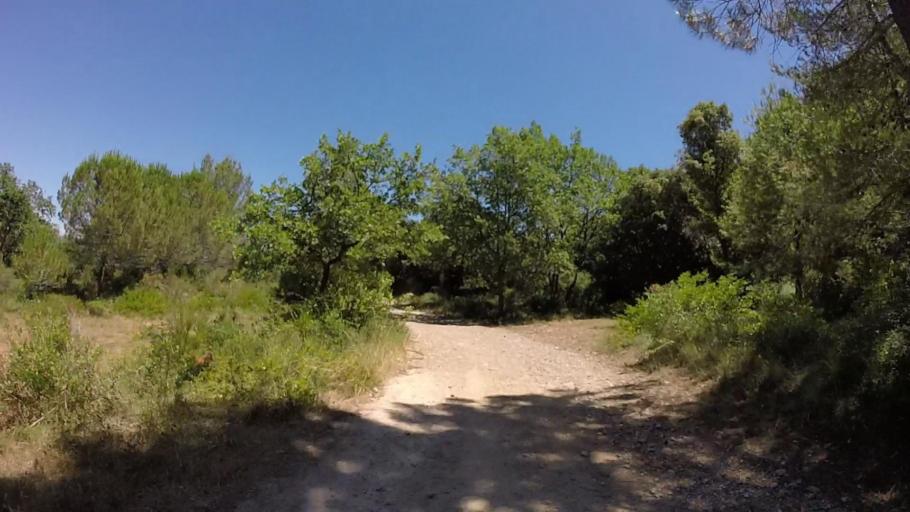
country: FR
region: Provence-Alpes-Cote d'Azur
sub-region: Departement des Alpes-Maritimes
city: Biot
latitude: 43.6303
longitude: 7.0480
